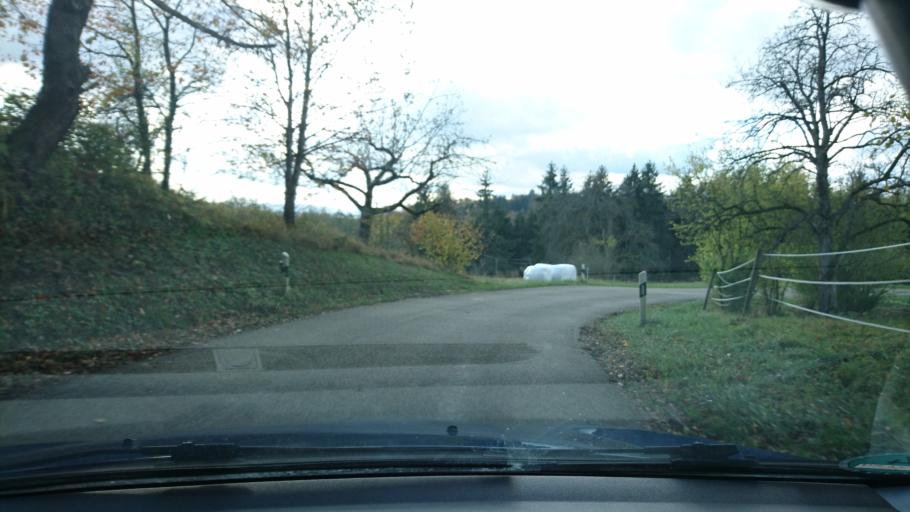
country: DE
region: Baden-Wuerttemberg
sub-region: Regierungsbezirk Stuttgart
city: Abtsgmund
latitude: 48.8781
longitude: 9.9715
